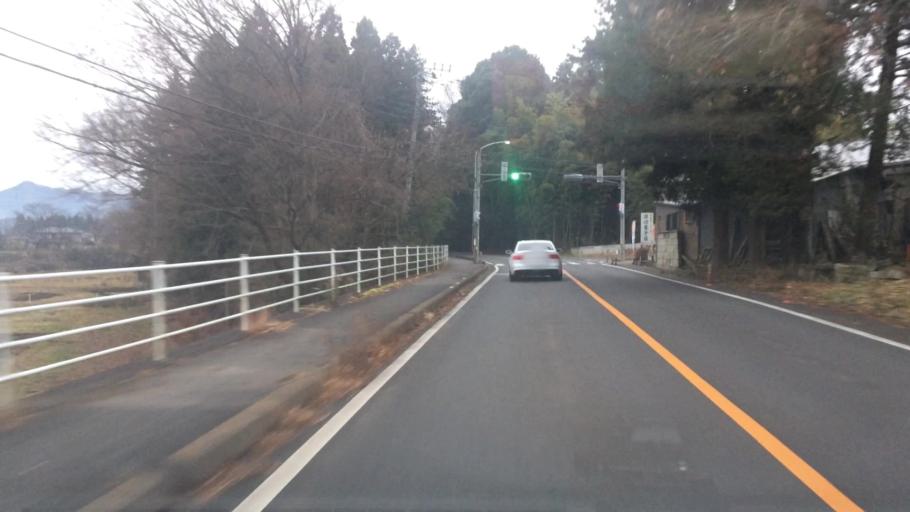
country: JP
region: Tochigi
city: Imaichi
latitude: 36.6723
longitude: 139.7725
